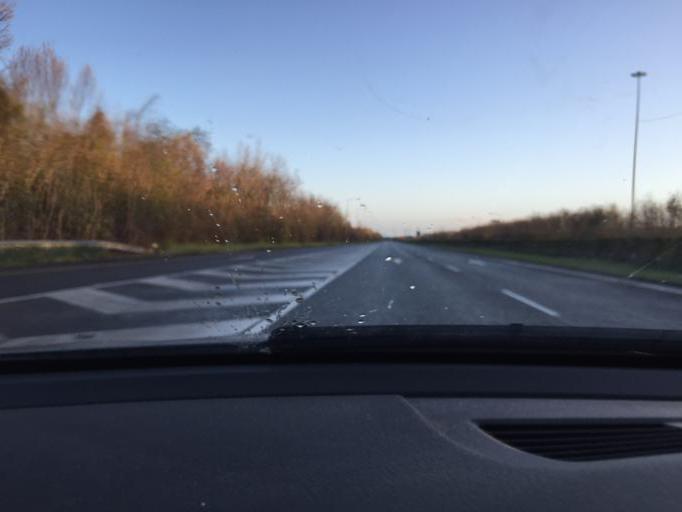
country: IE
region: Leinster
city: Balrothery
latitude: 53.5667
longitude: -6.2132
